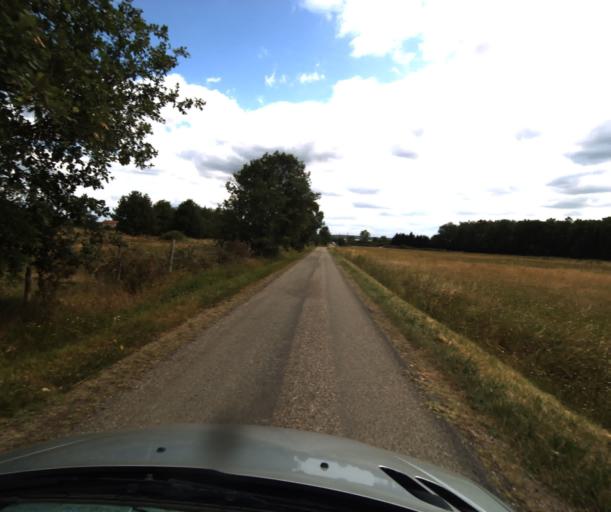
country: FR
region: Midi-Pyrenees
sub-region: Departement du Tarn-et-Garonne
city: Campsas
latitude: 43.9101
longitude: 1.3102
